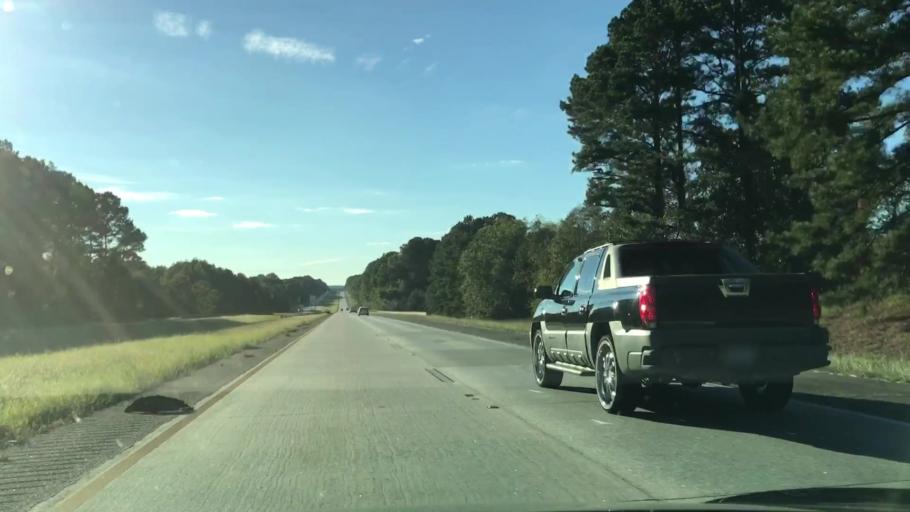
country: US
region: Georgia
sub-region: Greene County
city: Union Point
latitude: 33.5456
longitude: -83.0940
